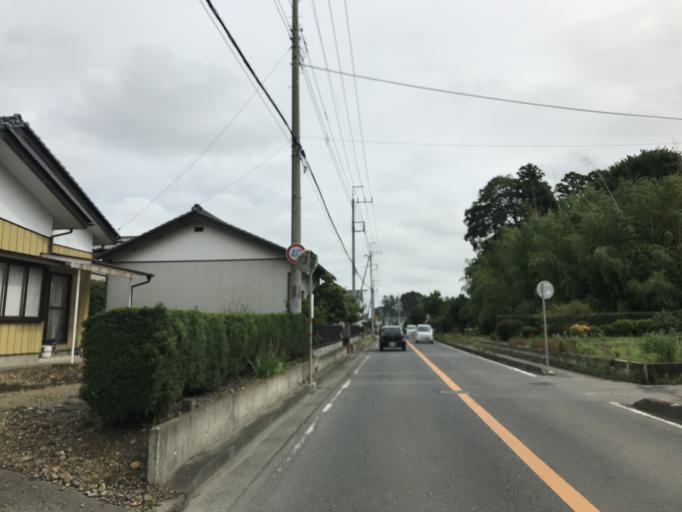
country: JP
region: Ibaraki
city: Mito-shi
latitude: 36.3311
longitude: 140.4564
